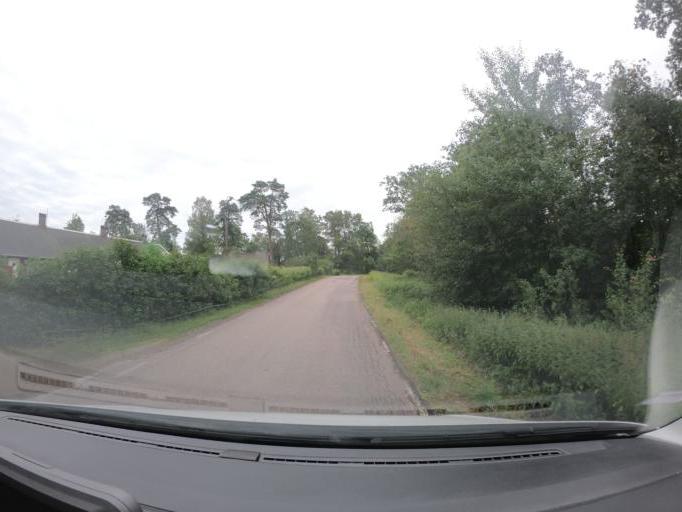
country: SE
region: Skane
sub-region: Angelholms Kommun
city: Munka-Ljungby
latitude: 56.3027
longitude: 13.0806
